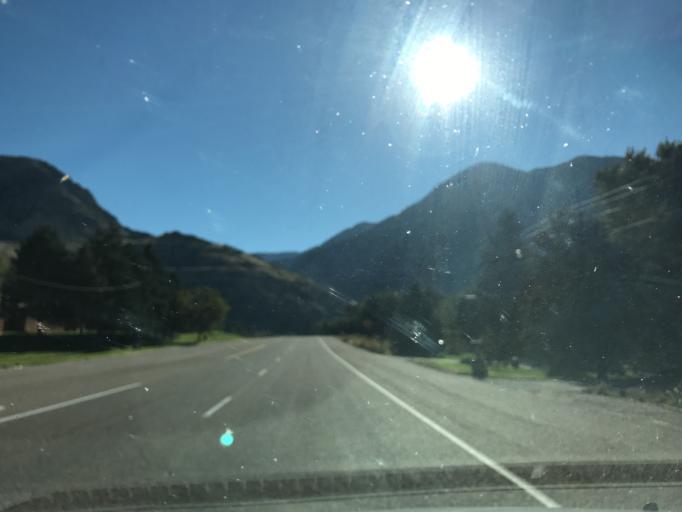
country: US
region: Utah
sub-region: Weber County
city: Ogden
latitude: 41.2398
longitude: -111.9370
